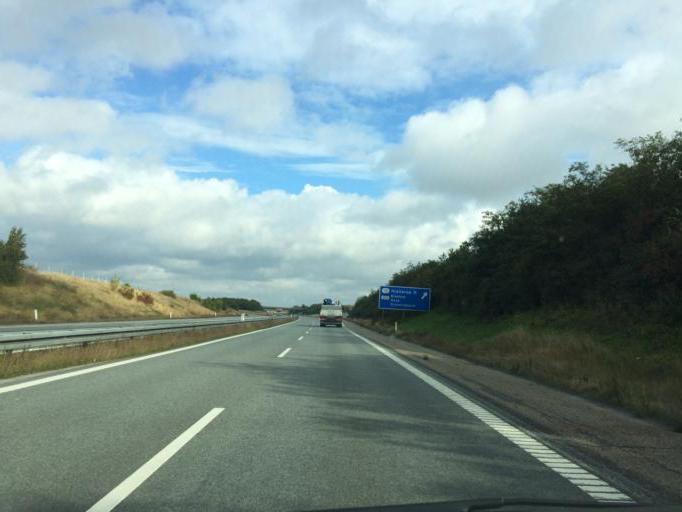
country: DK
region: North Denmark
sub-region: Bronderslev Kommune
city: Hjallerup
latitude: 57.1643
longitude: 10.1852
